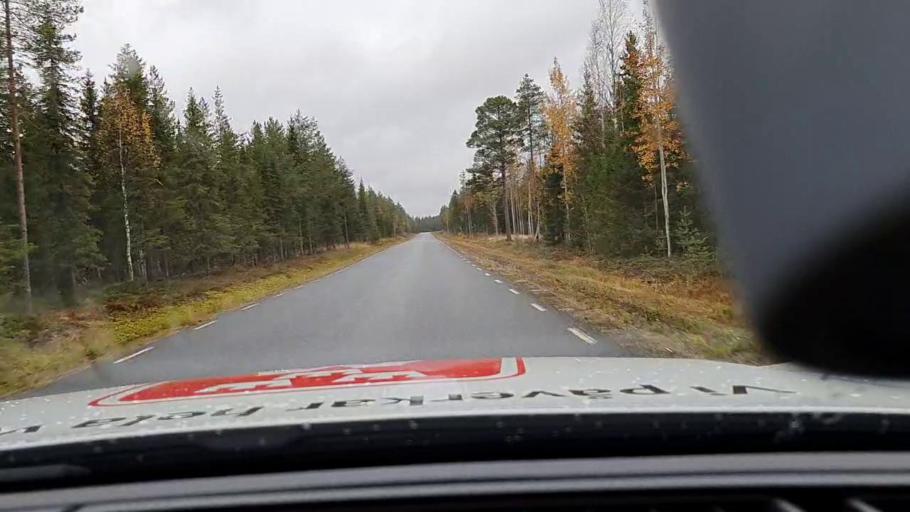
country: SE
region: Norrbotten
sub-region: Haparanda Kommun
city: Haparanda
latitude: 65.9357
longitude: 23.8109
